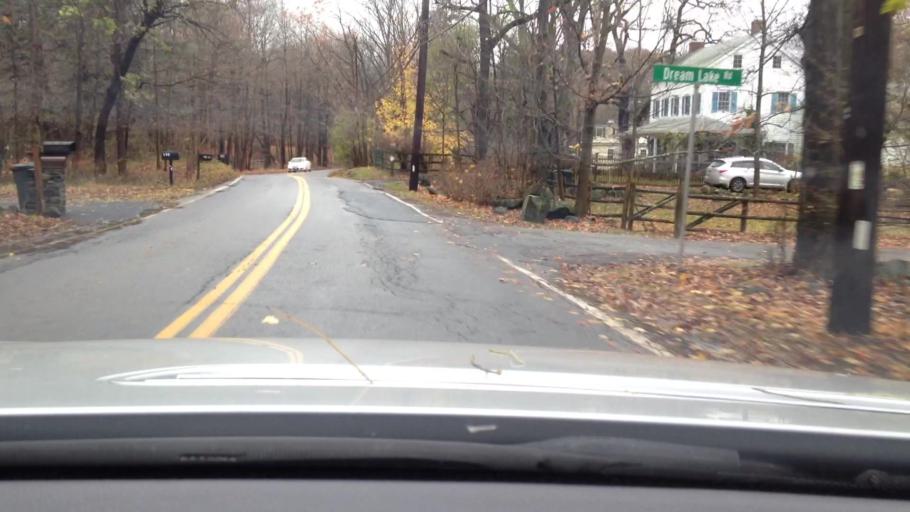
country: US
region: New York
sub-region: Westchester County
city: Croton-on-Hudson
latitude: 41.2272
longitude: -73.8767
